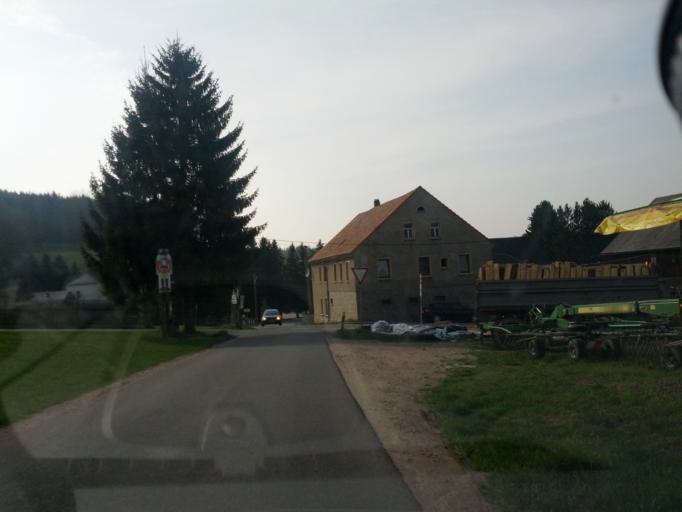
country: DE
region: Saxony
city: Kirchberg
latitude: 50.5900
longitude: 12.5188
